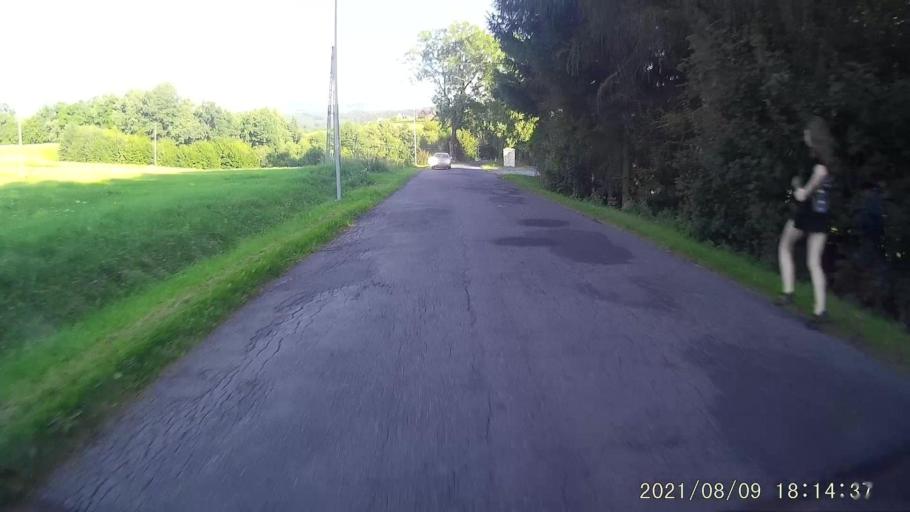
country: PL
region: Lower Silesian Voivodeship
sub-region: Powiat klodzki
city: Klodzko
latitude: 50.4968
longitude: 16.6624
